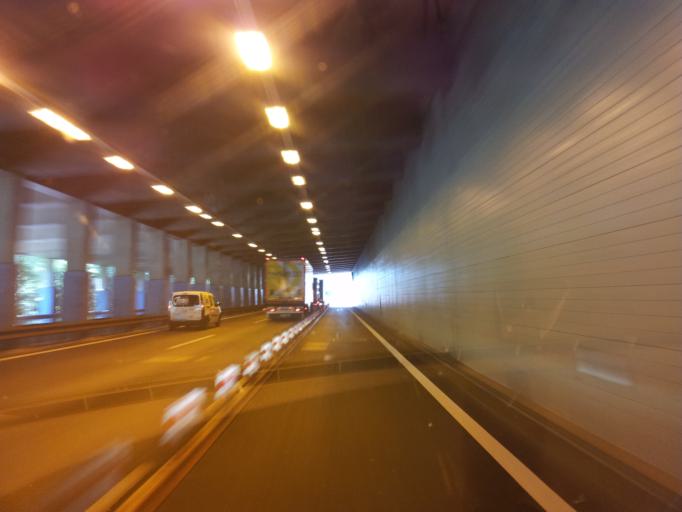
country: CH
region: Uri
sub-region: Uri
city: Andermatt
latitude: 46.6800
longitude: 8.5925
